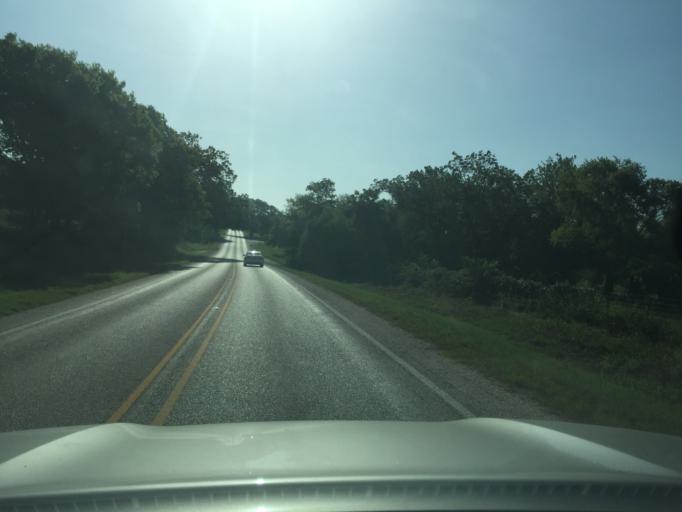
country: US
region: Texas
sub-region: Blanco County
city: Blanco
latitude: 30.0914
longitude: -98.3776
